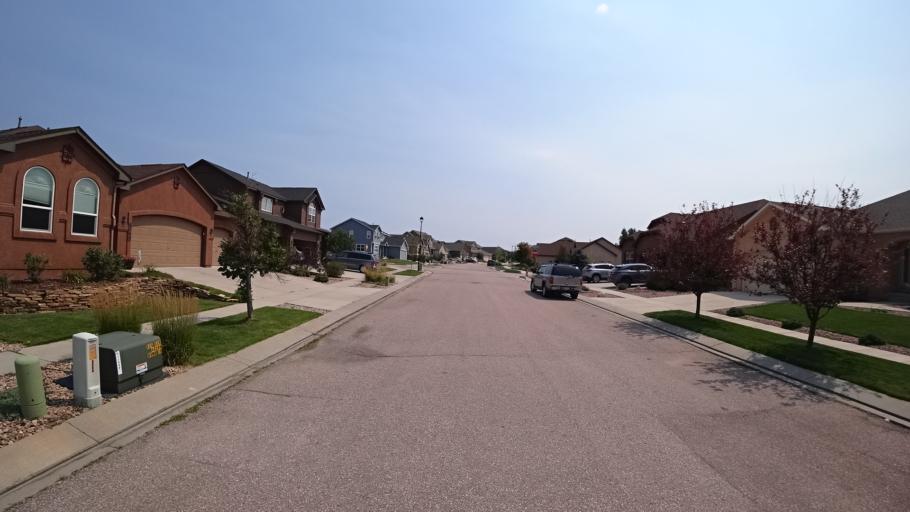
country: US
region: Colorado
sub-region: El Paso County
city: Black Forest
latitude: 38.9681
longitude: -104.7192
